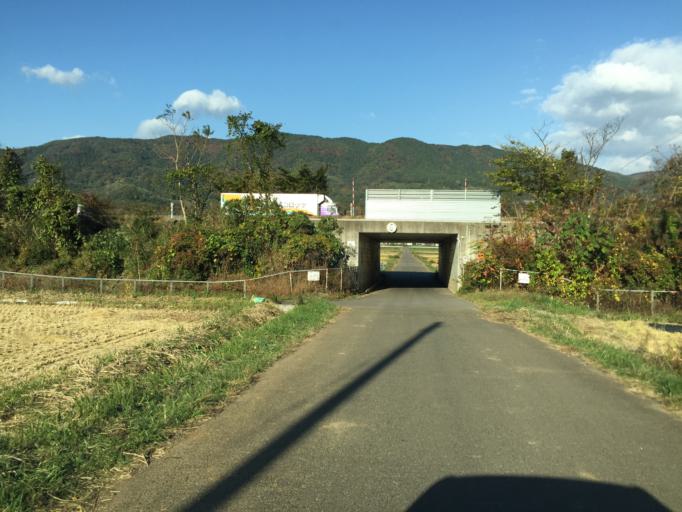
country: JP
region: Fukushima
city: Yanagawamachi-saiwaicho
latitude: 37.9236
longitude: 140.6100
